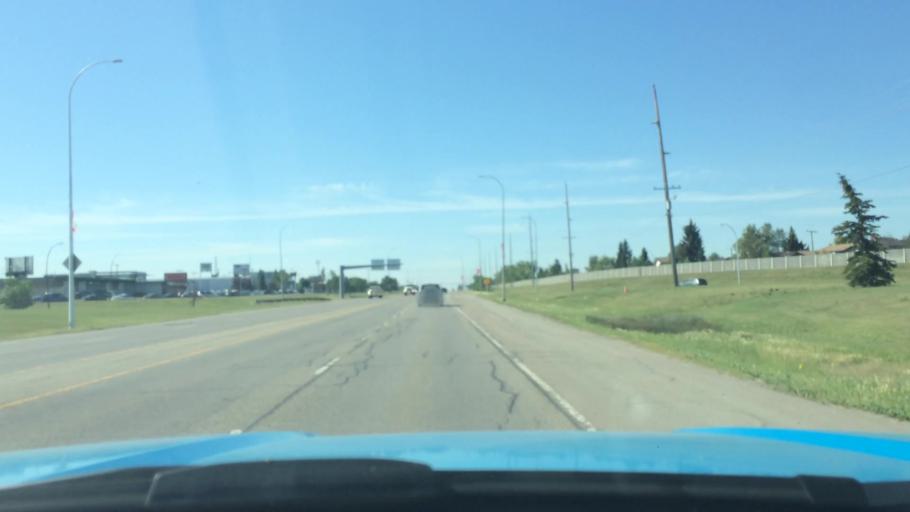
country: CA
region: Alberta
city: Calgary
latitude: 51.0652
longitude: -114.0018
